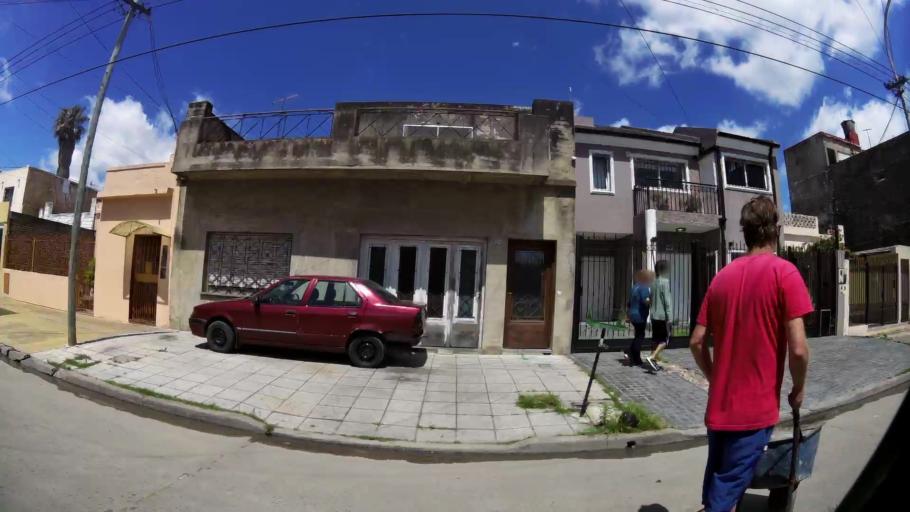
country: AR
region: Buenos Aires
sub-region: Partido de Lanus
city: Lanus
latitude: -34.6945
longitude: -58.4175
